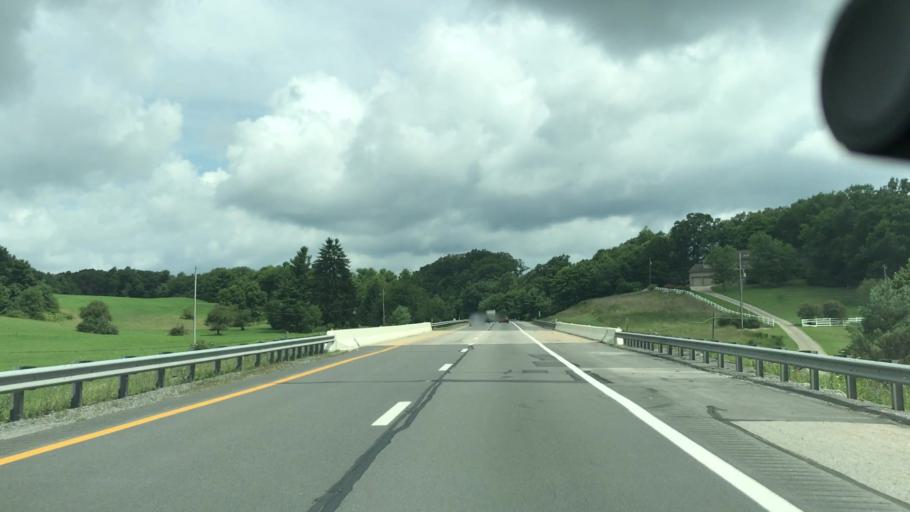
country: US
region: West Virginia
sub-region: Raleigh County
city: Shady Spring
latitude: 37.6498
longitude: -81.1086
